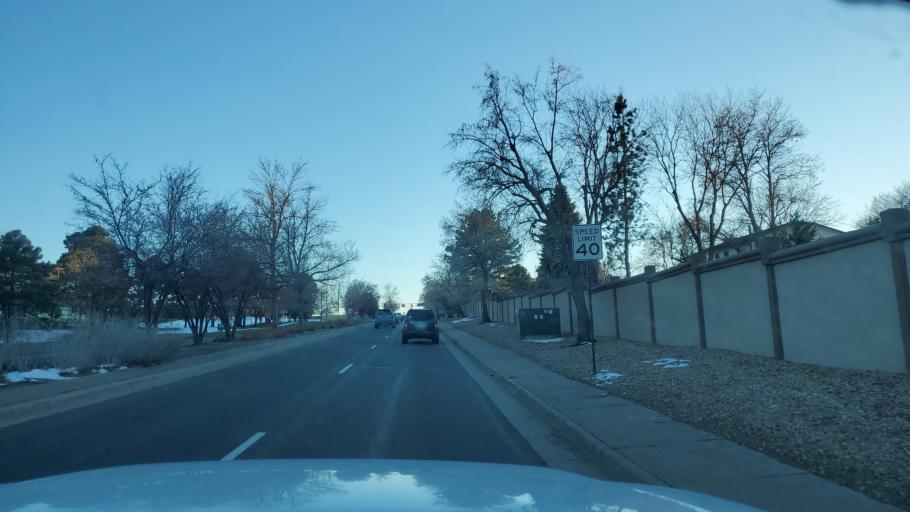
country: US
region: Colorado
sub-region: Arapahoe County
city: Castlewood
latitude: 39.6050
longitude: -104.9042
